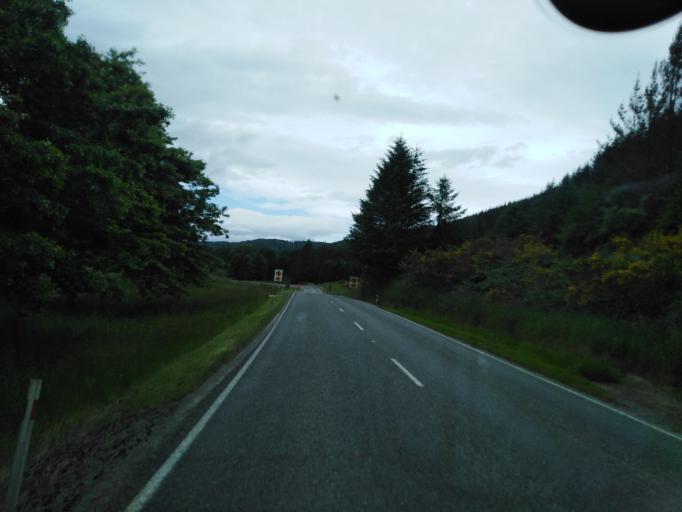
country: NZ
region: Tasman
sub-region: Tasman District
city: Wakefield
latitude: -41.4851
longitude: 172.8879
